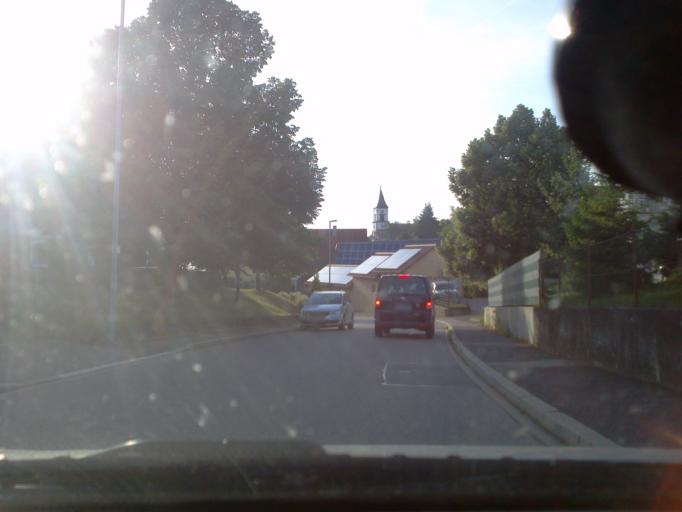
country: DE
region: Baden-Wuerttemberg
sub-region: Karlsruhe Region
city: Woessingen
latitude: 49.0092
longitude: 8.6145
